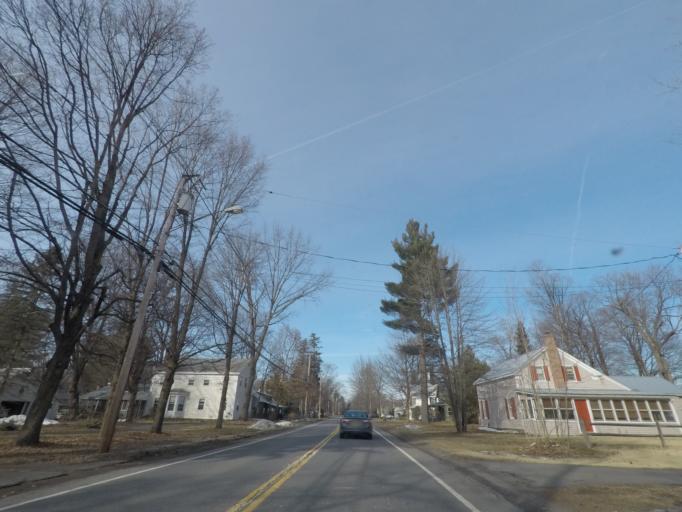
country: US
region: New York
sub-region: Columbia County
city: Niverville
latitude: 42.4713
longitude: -73.6318
